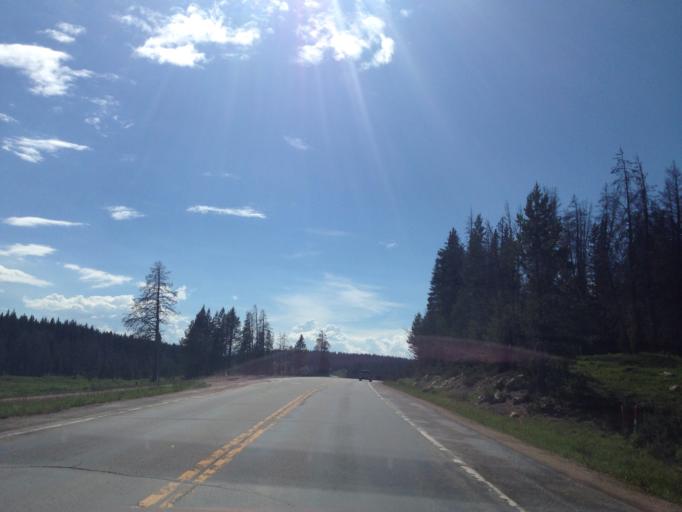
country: US
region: Colorado
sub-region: Routt County
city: Steamboat Springs
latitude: 40.3888
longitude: -106.6590
